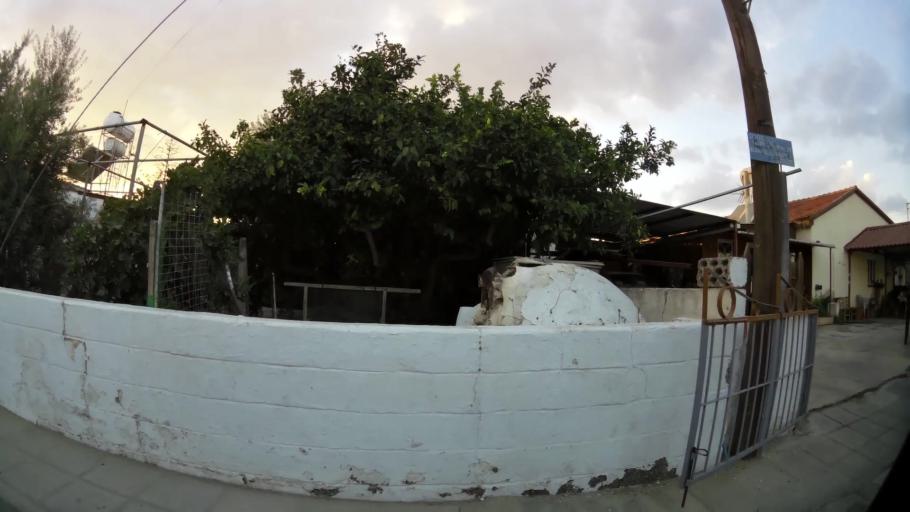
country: CY
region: Larnaka
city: Meneou
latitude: 34.8661
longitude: 33.5878
